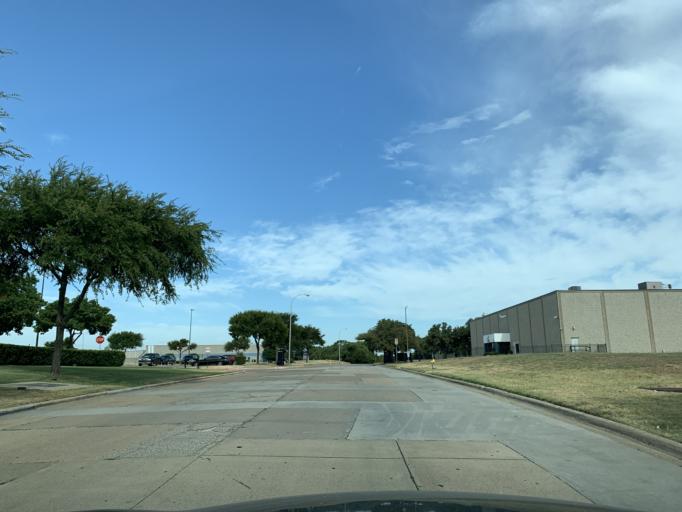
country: US
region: Texas
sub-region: Dallas County
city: Cockrell Hill
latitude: 32.7699
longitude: -96.8674
